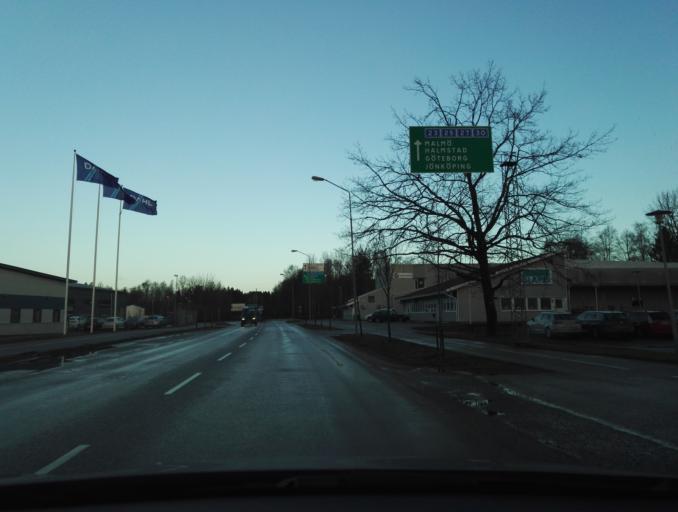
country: SE
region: Kronoberg
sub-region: Vaxjo Kommun
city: Vaexjoe
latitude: 56.8940
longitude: 14.7821
